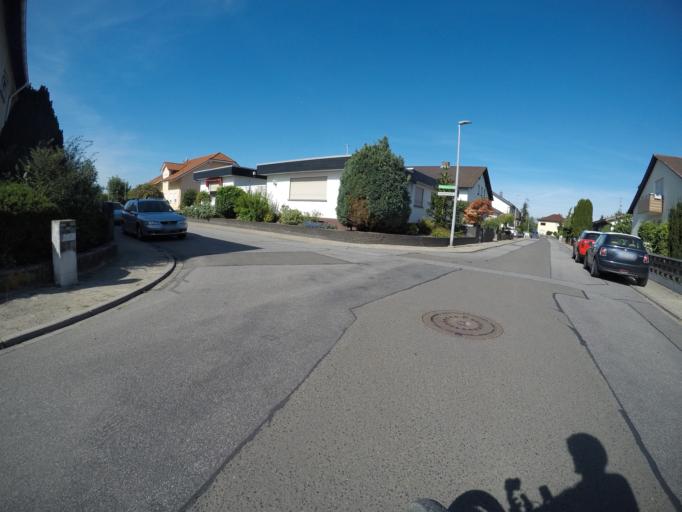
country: DE
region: Hesse
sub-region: Regierungsbezirk Darmstadt
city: Biblis
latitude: 49.6935
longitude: 8.4593
